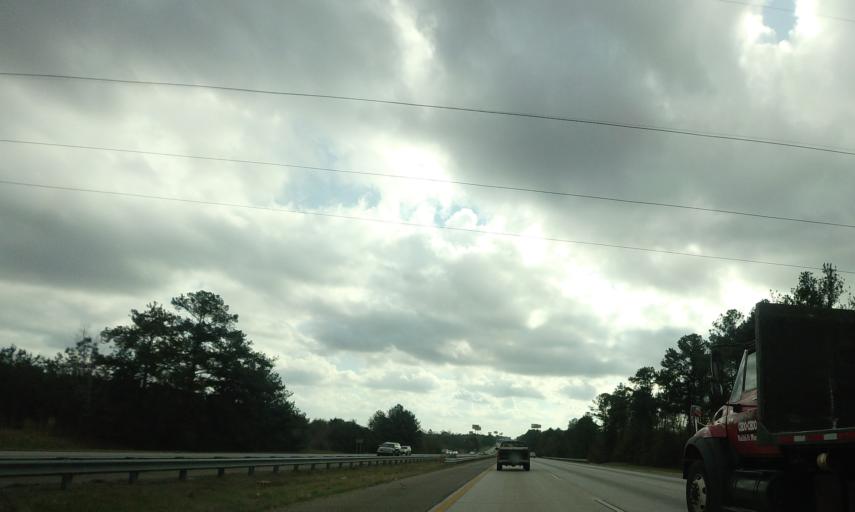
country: US
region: Georgia
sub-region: Peach County
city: Byron
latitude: 32.6269
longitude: -83.7430
